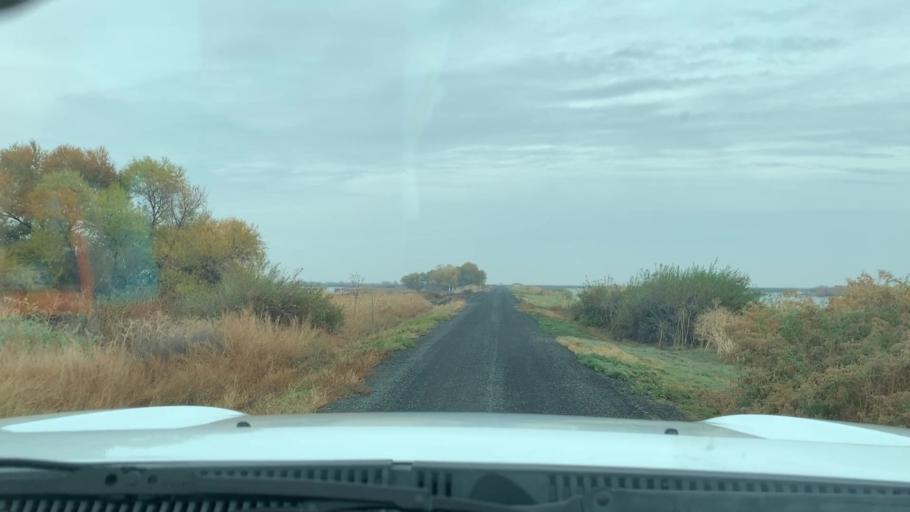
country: US
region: California
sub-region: Tulare County
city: Alpaugh
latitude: 35.7488
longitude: -119.5857
